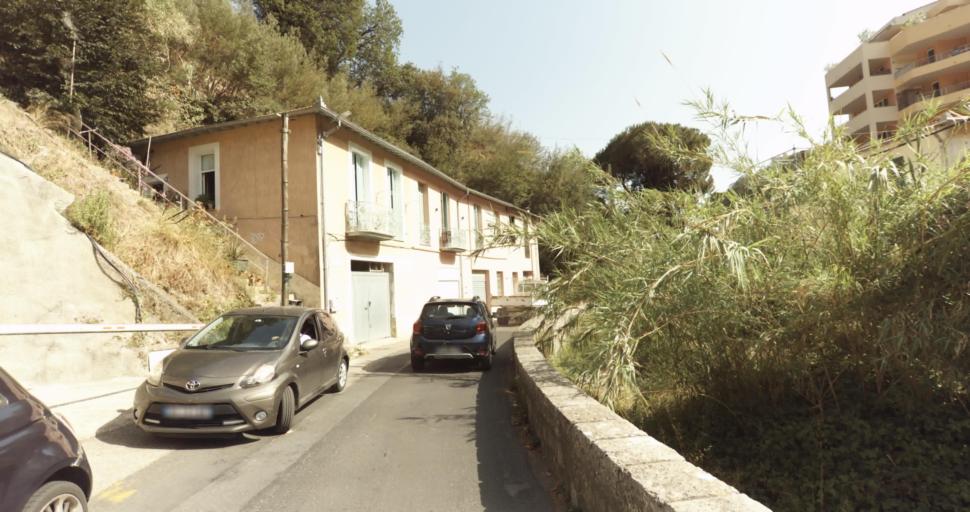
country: FR
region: Provence-Alpes-Cote d'Azur
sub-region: Departement des Alpes-Maritimes
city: Roquebrune-Cap-Martin
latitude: 43.7851
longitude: 7.4847
